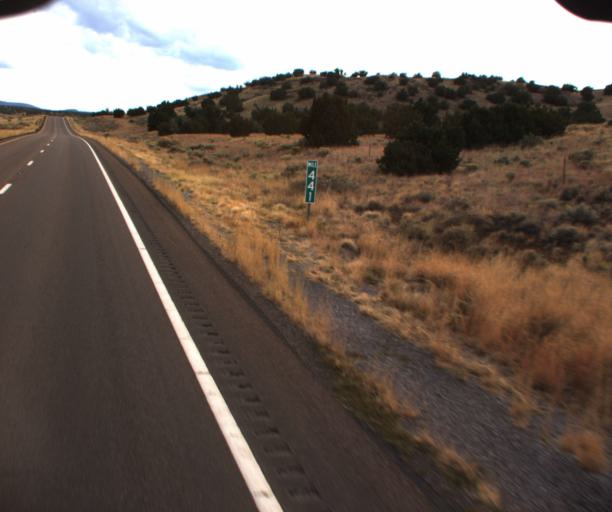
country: US
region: Arizona
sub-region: Coconino County
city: Flagstaff
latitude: 35.5211
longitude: -111.5438
